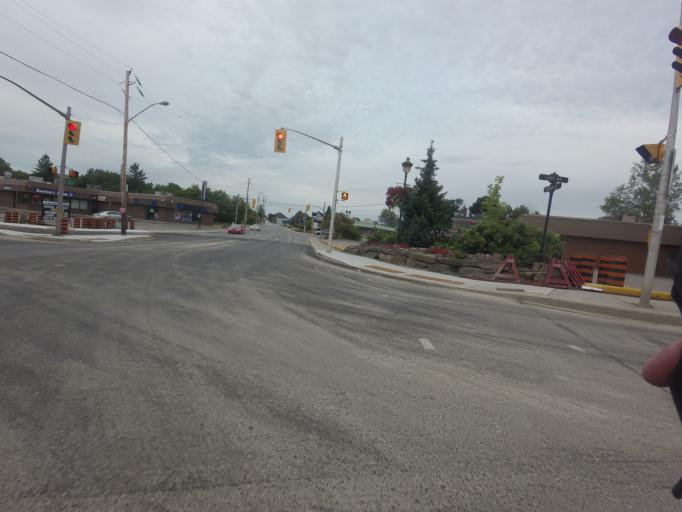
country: CA
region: Ontario
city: Carleton Place
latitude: 45.1369
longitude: -76.1422
